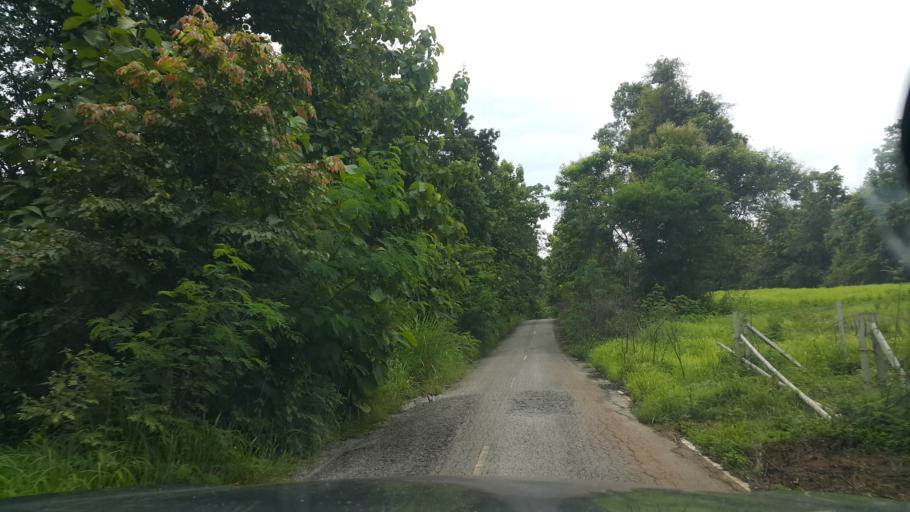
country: TH
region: Chiang Mai
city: Mae On
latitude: 18.8252
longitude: 99.2345
